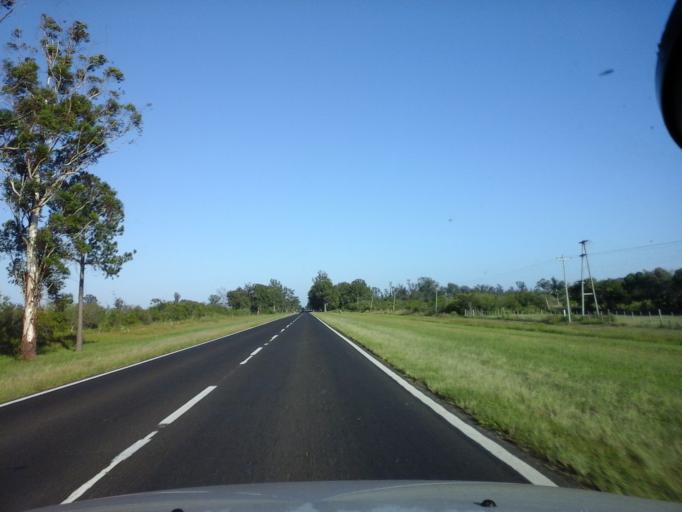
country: AR
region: Corrientes
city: Ita Ibate
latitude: -27.4594
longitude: -57.3178
